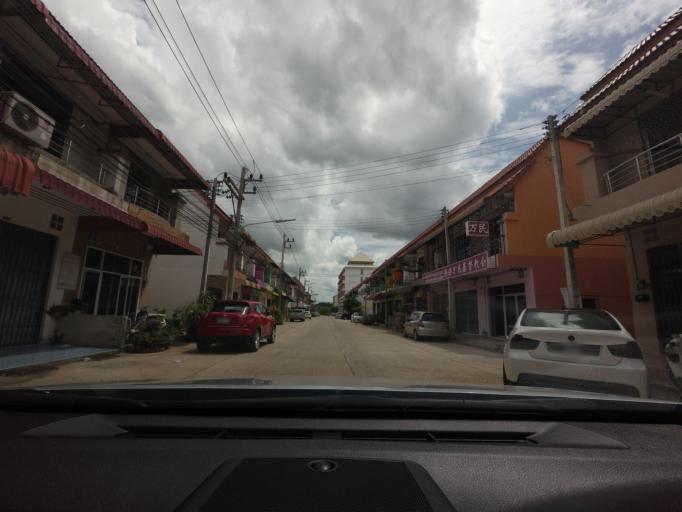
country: TH
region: Songkhla
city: Sadao
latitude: 6.5311
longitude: 100.4159
